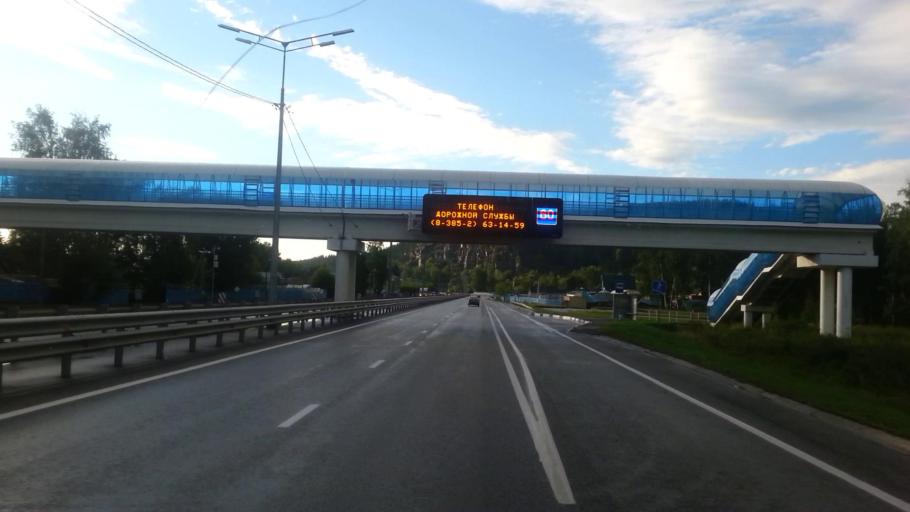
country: RU
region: Altay
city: Souzga
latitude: 51.9142
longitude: 85.8631
